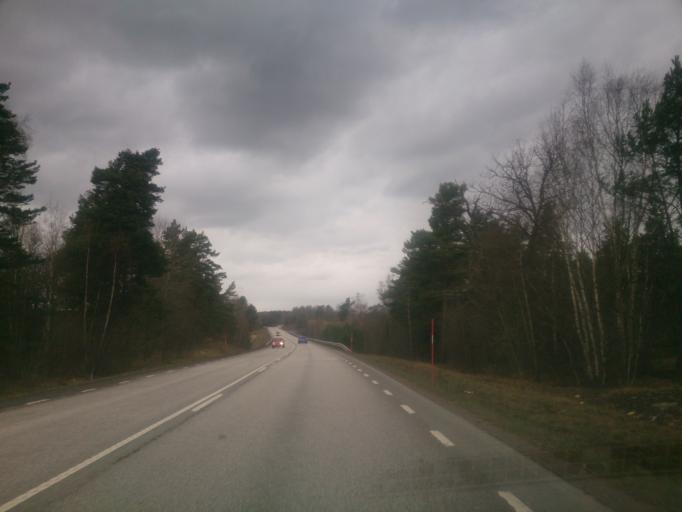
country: SE
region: OEstergoetland
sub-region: Norrkopings Kommun
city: Svartinge
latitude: 58.5746
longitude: 16.0568
